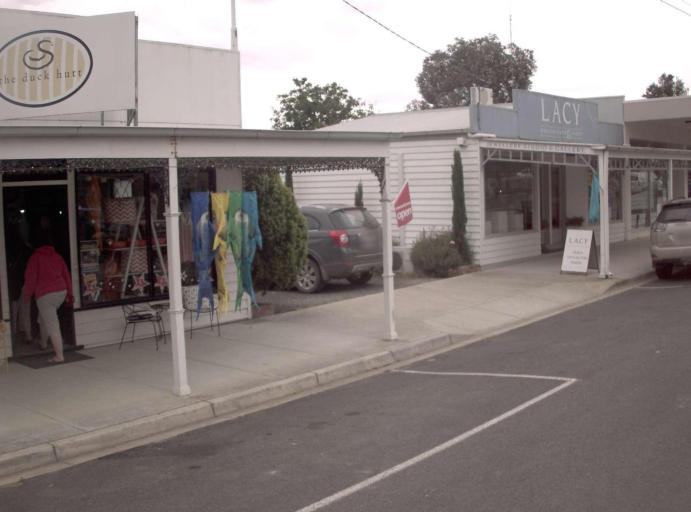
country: AU
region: Victoria
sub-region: Bass Coast
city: North Wonthaggi
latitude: -38.5784
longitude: 146.0128
